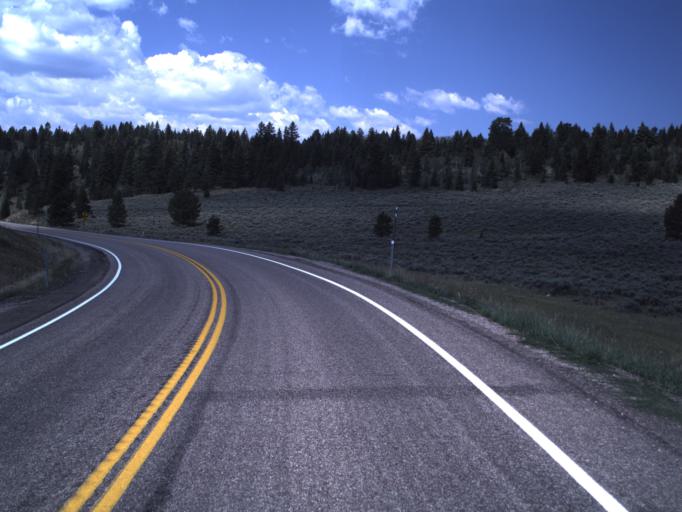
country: US
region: Utah
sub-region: Uintah County
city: Maeser
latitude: 40.7160
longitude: -109.4847
